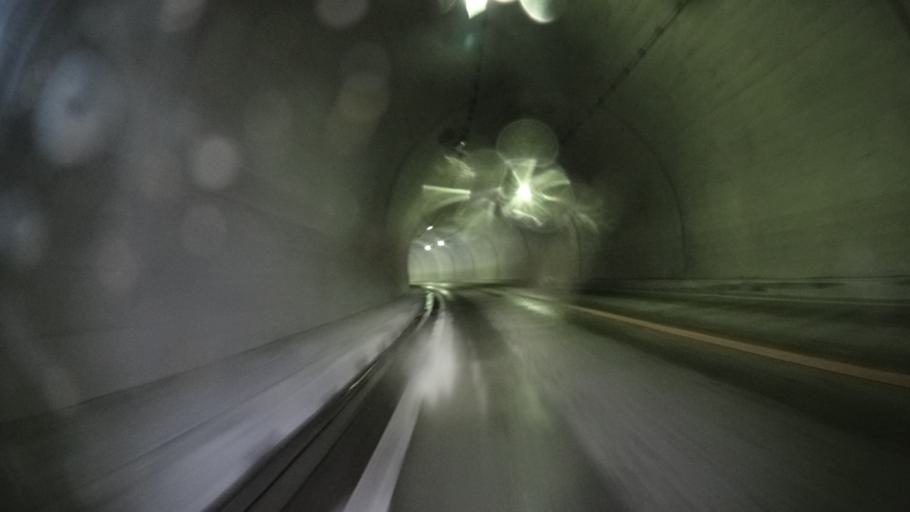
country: JP
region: Yamanashi
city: Enzan
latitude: 35.8068
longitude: 138.8611
